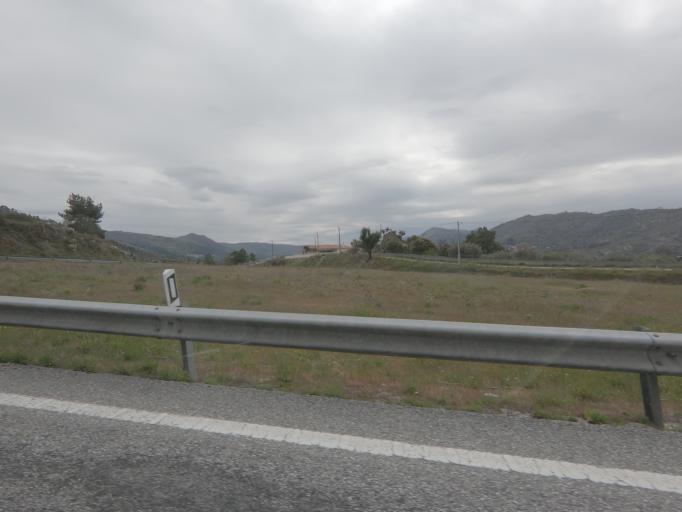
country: PT
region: Guarda
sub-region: Guarda
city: Guarda
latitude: 40.6194
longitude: -7.2871
